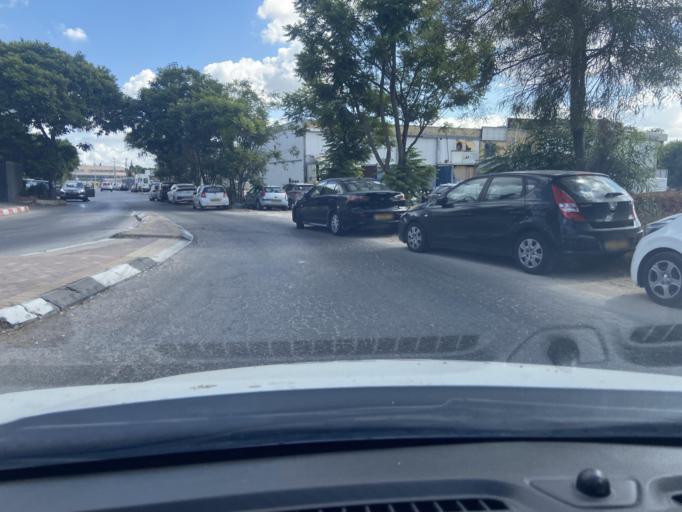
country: IL
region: Central District
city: Yehud
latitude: 32.0267
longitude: 34.8935
